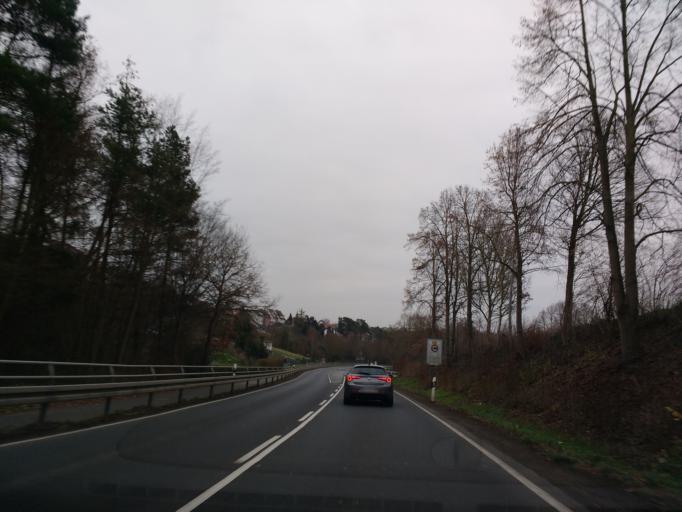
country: DE
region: Hesse
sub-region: Regierungsbezirk Kassel
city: Baunatal
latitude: 51.2166
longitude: 9.4348
